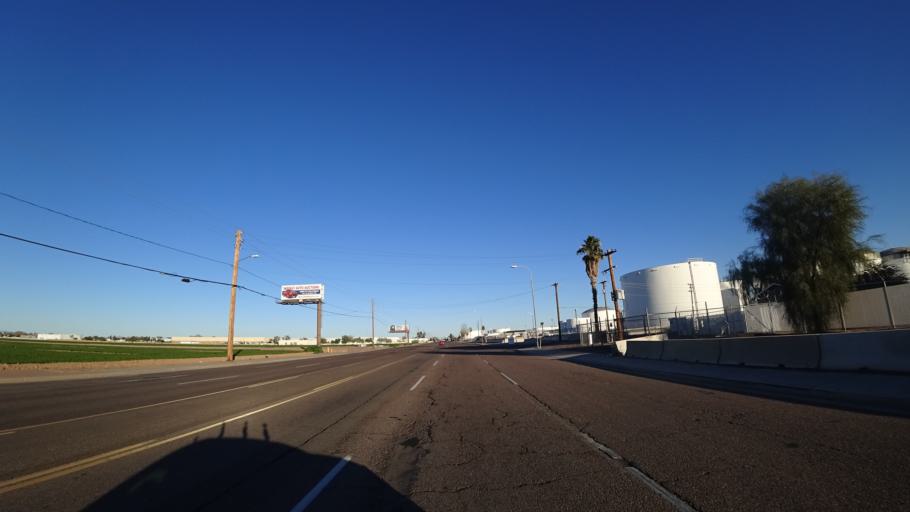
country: US
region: Arizona
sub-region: Maricopa County
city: Tolleson
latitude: 33.4512
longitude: -112.1786
